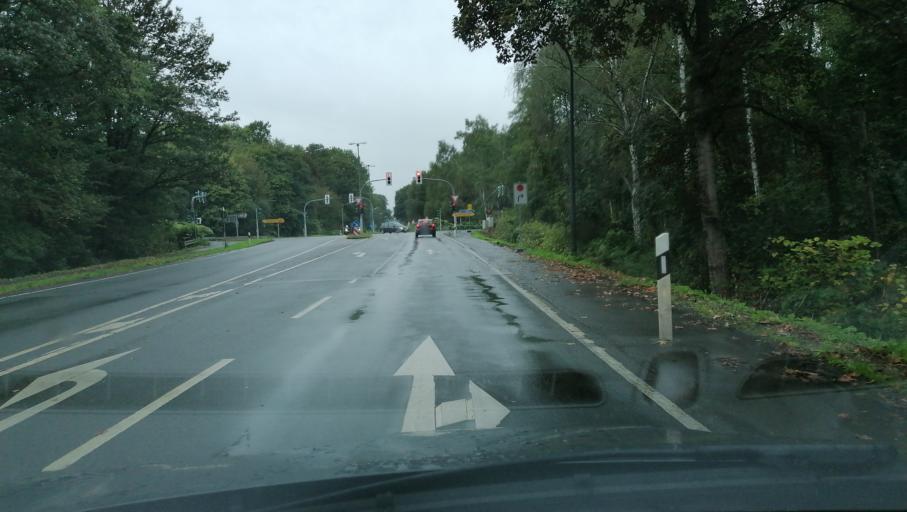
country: DE
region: North Rhine-Westphalia
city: Herten
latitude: 51.5675
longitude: 7.1289
